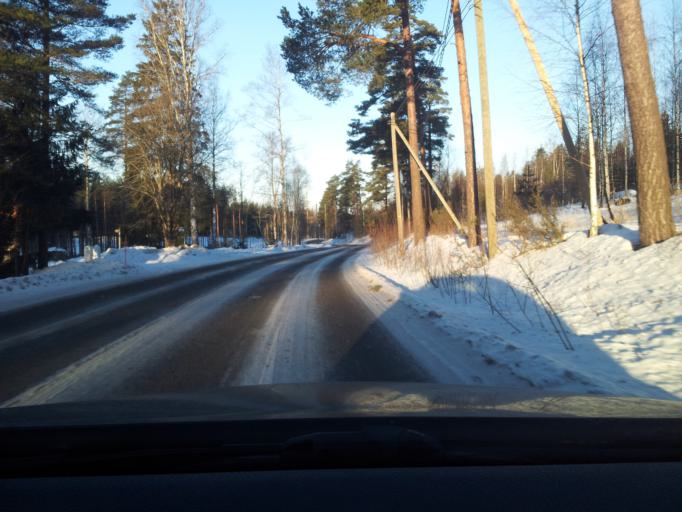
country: FI
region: Uusimaa
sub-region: Helsinki
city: Vihti
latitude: 60.3738
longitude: 24.3678
